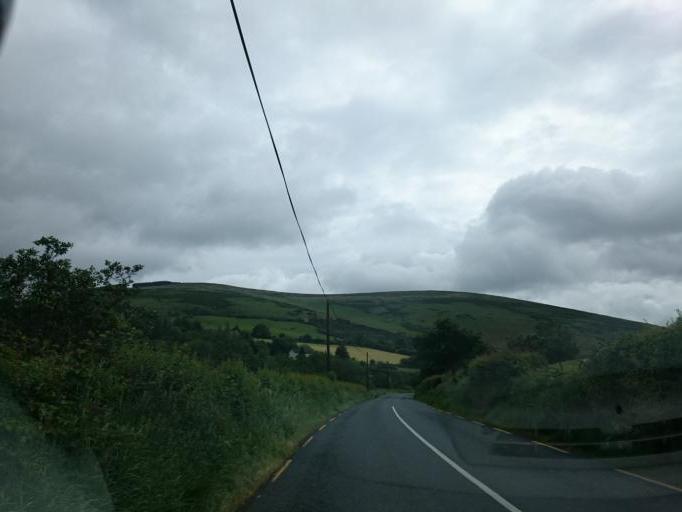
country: IE
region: Leinster
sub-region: Wicklow
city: Carnew
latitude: 52.8164
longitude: -6.4974
